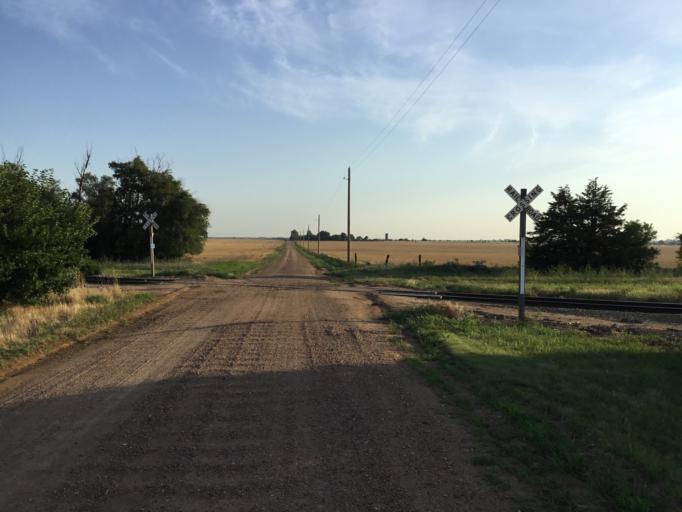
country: US
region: Kansas
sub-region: Sedgwick County
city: Cheney
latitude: 37.4603
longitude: -97.8623
